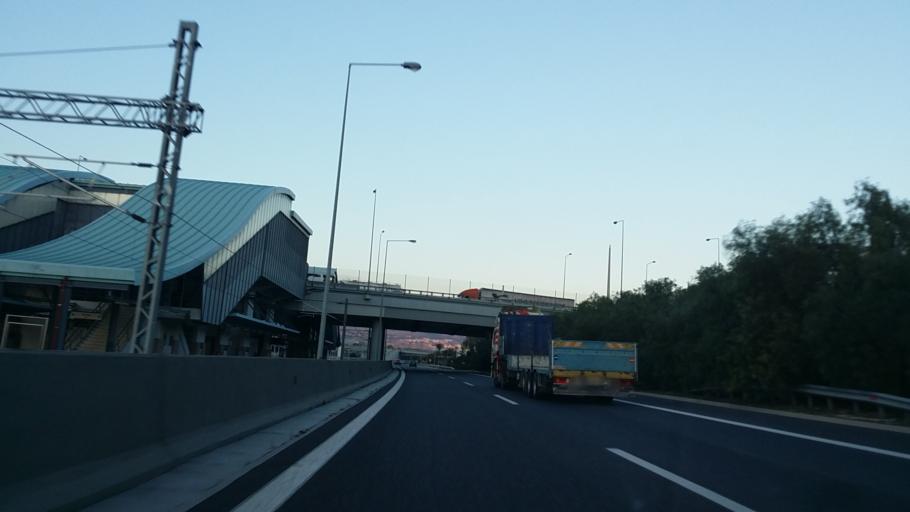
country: GR
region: Attica
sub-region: Nomarchia Dytikis Attikis
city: Magoula
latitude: 38.0726
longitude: 23.5291
